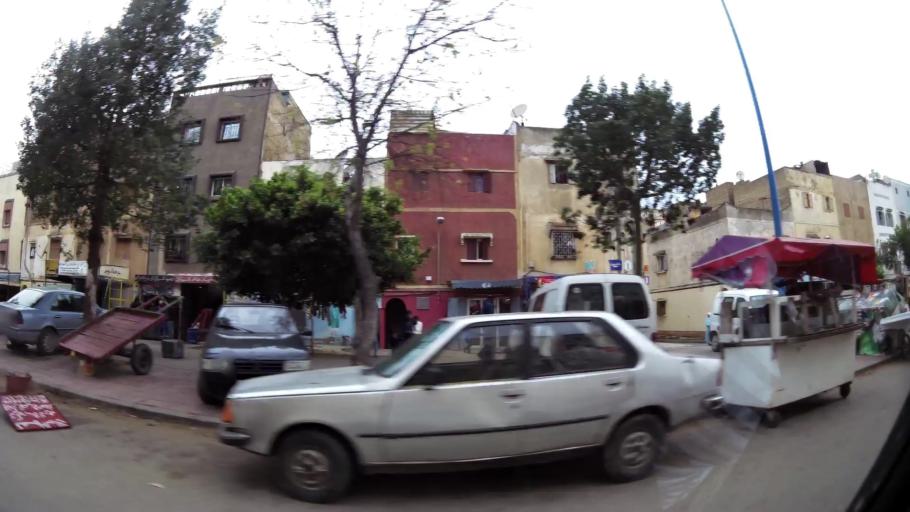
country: MA
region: Grand Casablanca
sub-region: Mediouna
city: Tit Mellil
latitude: 33.5621
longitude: -7.5412
